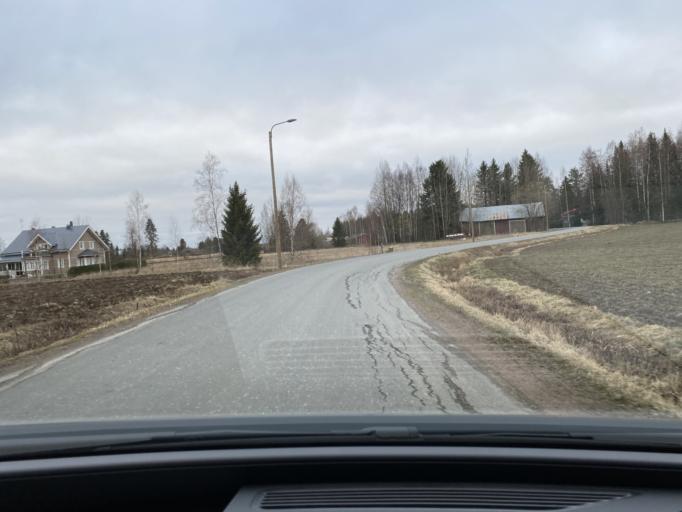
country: FI
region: Satakunta
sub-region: Pori
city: Huittinen
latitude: 61.1666
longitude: 22.7219
